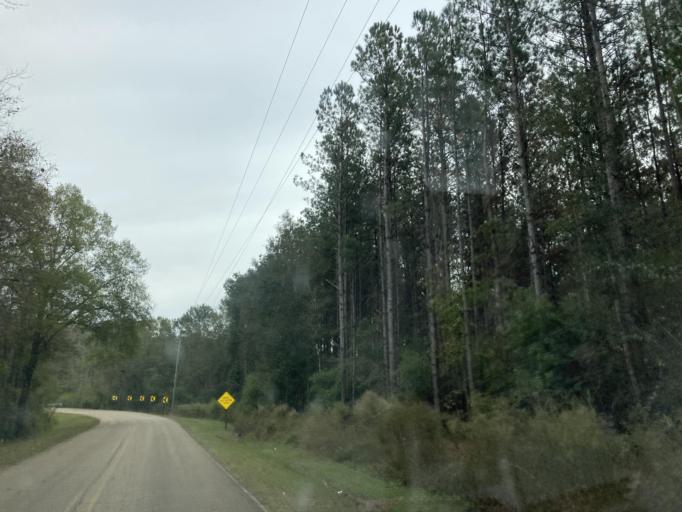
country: US
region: Mississippi
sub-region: Lamar County
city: Lumberton
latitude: 31.0321
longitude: -89.4617
